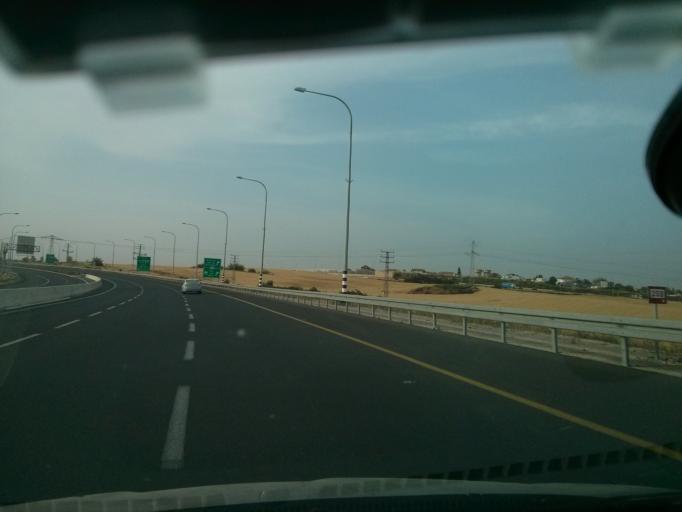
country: IL
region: Central District
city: Bene 'Ayish
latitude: 31.7993
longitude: 34.7640
